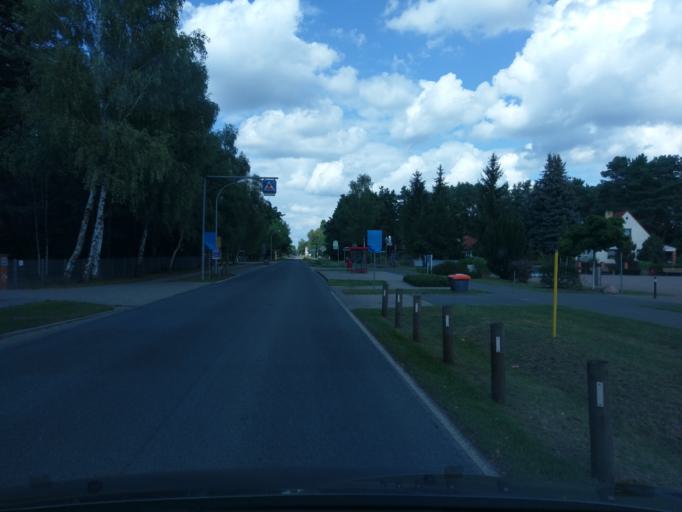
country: DE
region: Brandenburg
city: Borkheide
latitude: 52.2253
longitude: 12.8575
